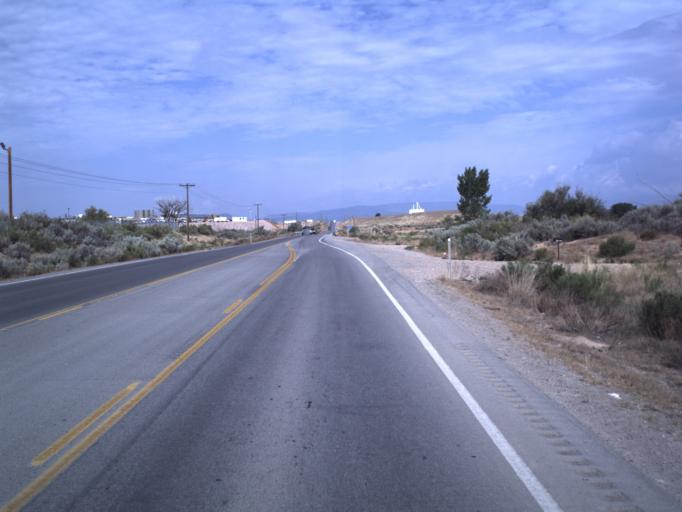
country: US
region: Utah
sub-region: Uintah County
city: Naples
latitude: 40.3902
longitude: -109.4429
